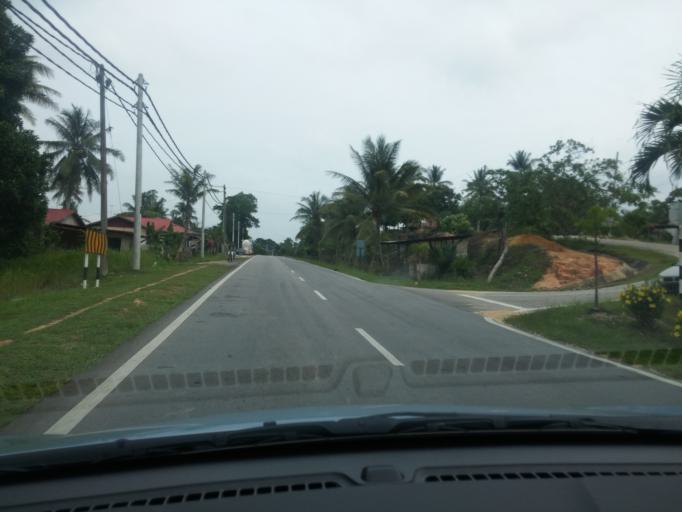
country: MY
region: Pahang
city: Kuantan
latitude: 3.8394
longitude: 103.1614
